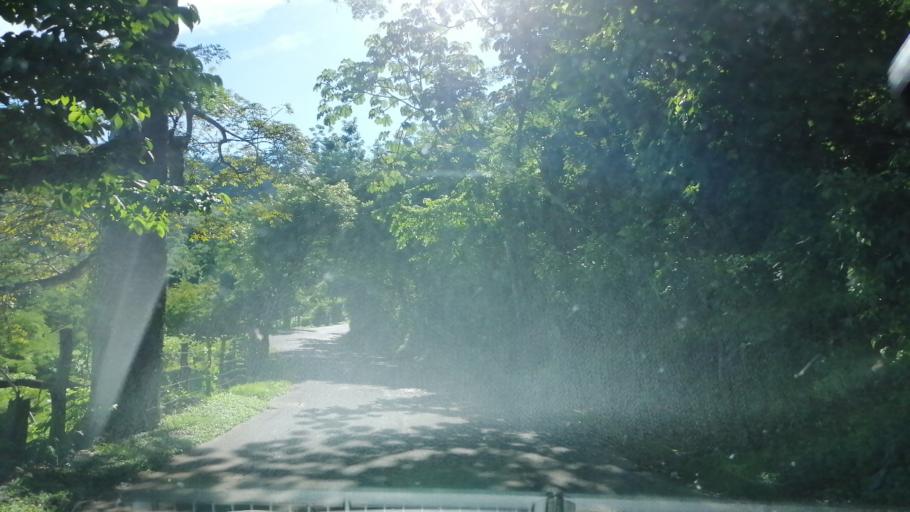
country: SV
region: Morazan
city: Corinto
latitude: 13.7901
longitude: -88.0255
